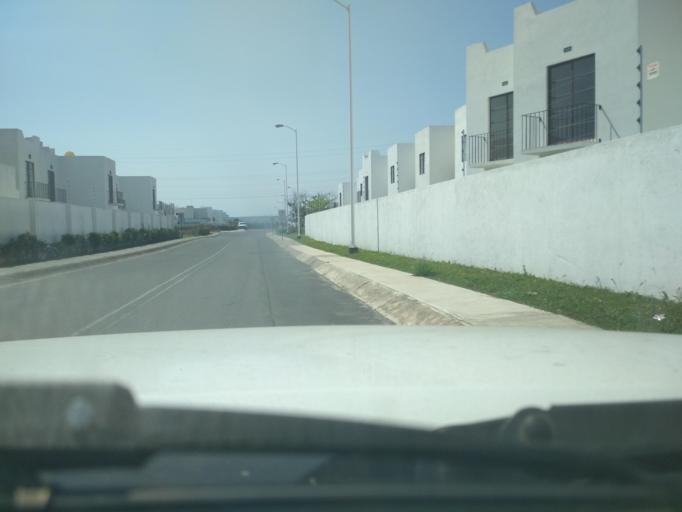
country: MX
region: Veracruz
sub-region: Veracruz
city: Lomas de Rio Medio Cuatro
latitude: 19.1799
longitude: -96.1906
